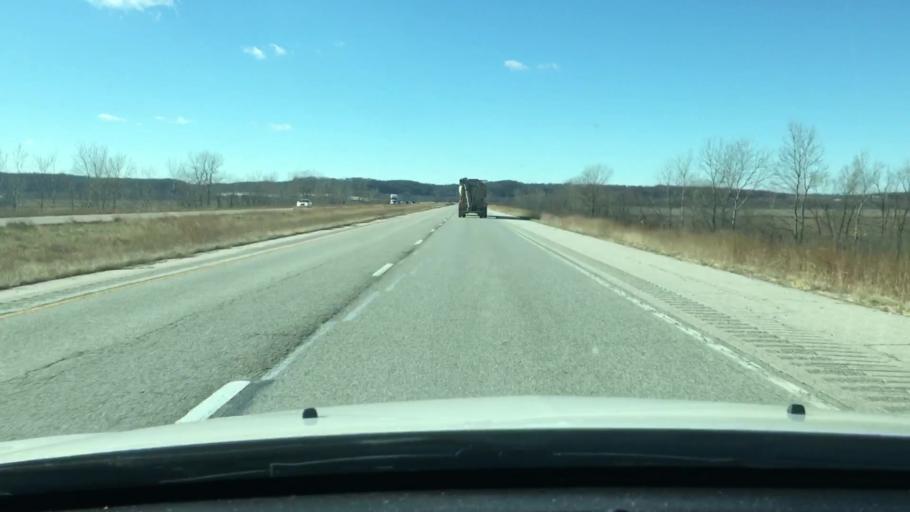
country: US
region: Illinois
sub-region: Pike County
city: Griggsville
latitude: 39.6920
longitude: -90.6136
